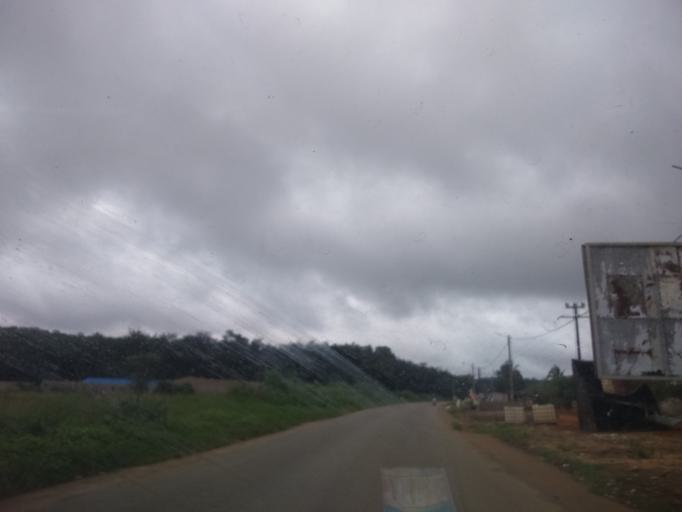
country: CI
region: Sud-Comoe
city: Bonoua
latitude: 5.2820
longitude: -3.5138
